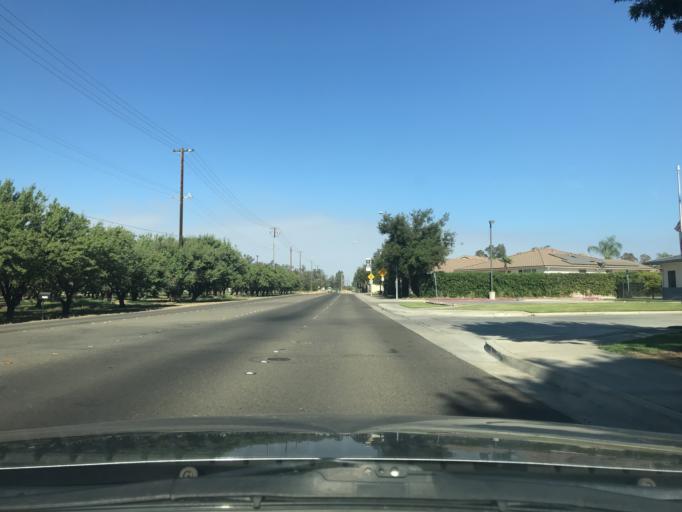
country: US
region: California
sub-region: Merced County
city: Atwater
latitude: 37.3495
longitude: -120.5705
